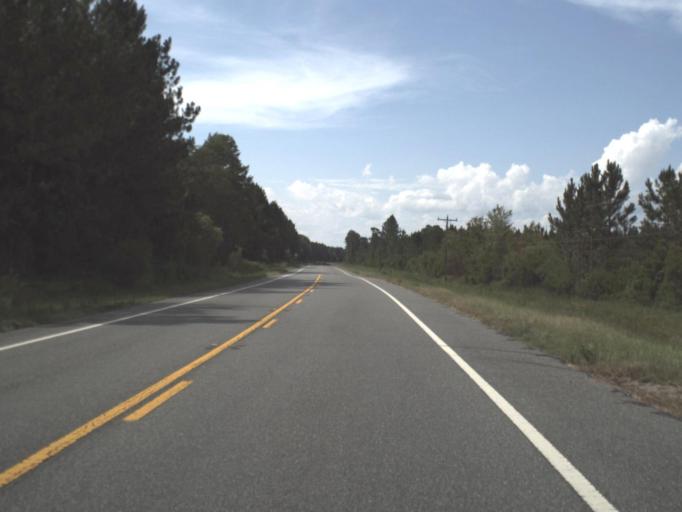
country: US
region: Florida
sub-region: Taylor County
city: Perry
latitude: 30.2050
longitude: -83.6079
